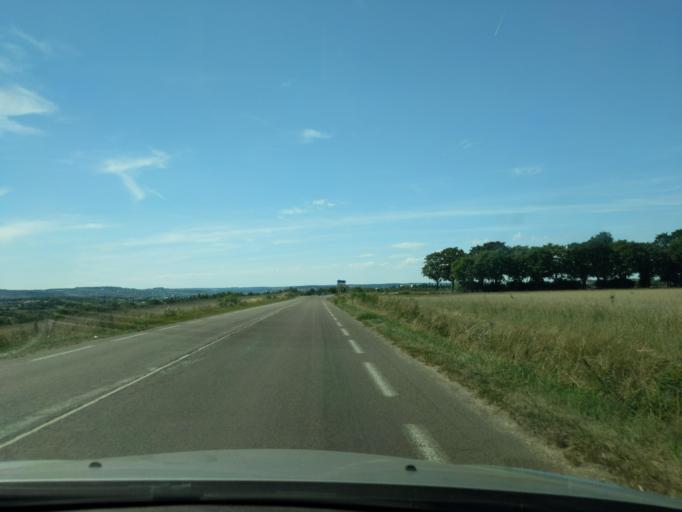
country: FR
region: Bourgogne
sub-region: Departement de la Cote-d'Or
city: Sennecey-les-Dijon
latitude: 47.2945
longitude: 5.0861
